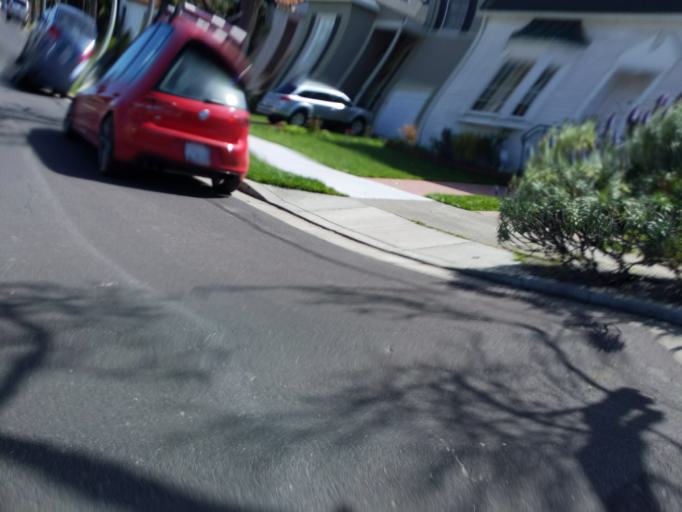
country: US
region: California
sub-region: Alameda County
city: Alameda
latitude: 37.7664
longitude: -122.2312
